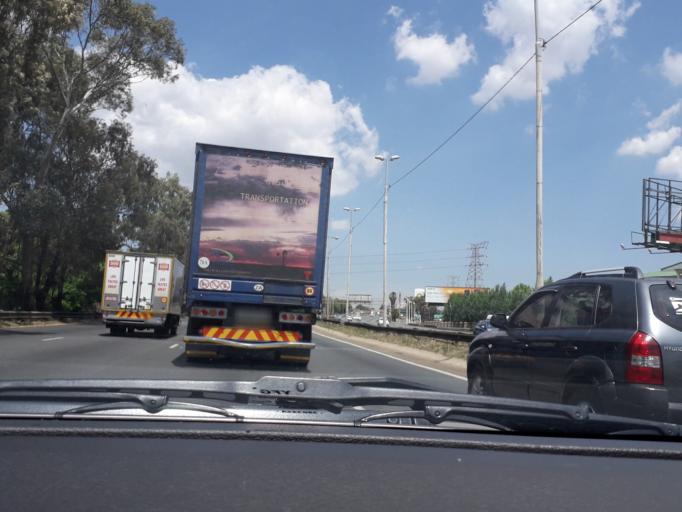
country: ZA
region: Gauteng
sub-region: City of Johannesburg Metropolitan Municipality
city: Johannesburg
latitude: -26.2397
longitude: 28.0146
